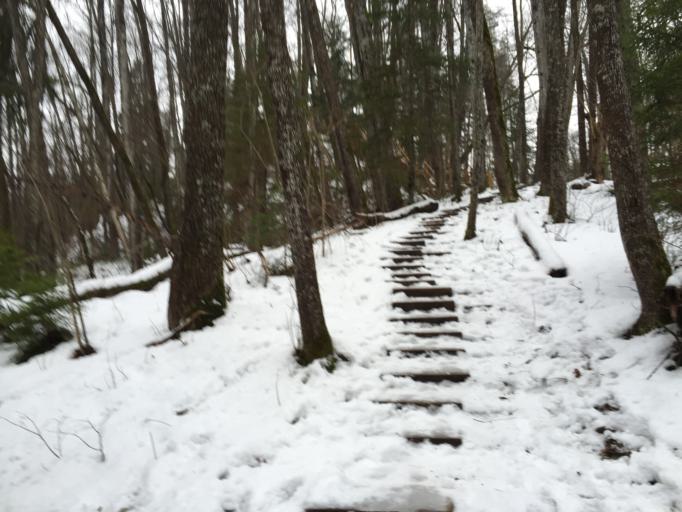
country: LV
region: Sigulda
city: Sigulda
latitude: 57.1743
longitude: 24.8668
